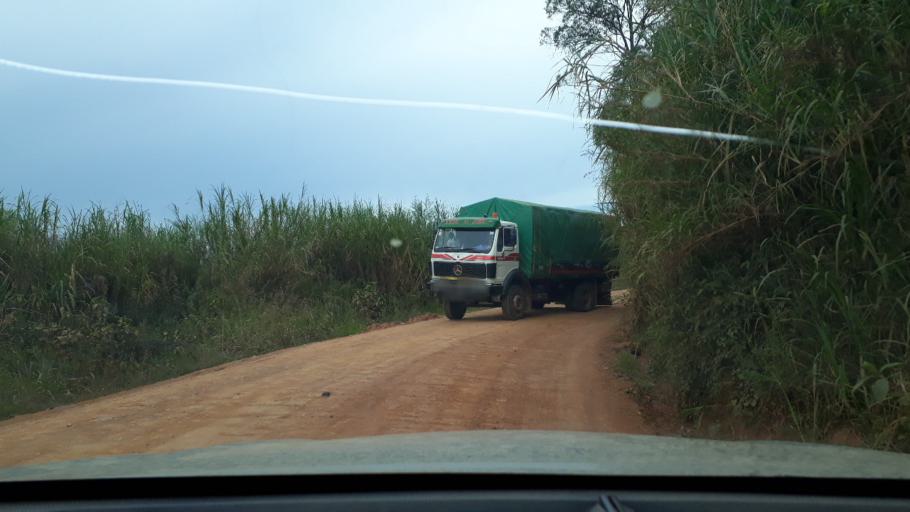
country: CD
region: Eastern Province
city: Bunia
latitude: 1.8073
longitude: 30.4095
